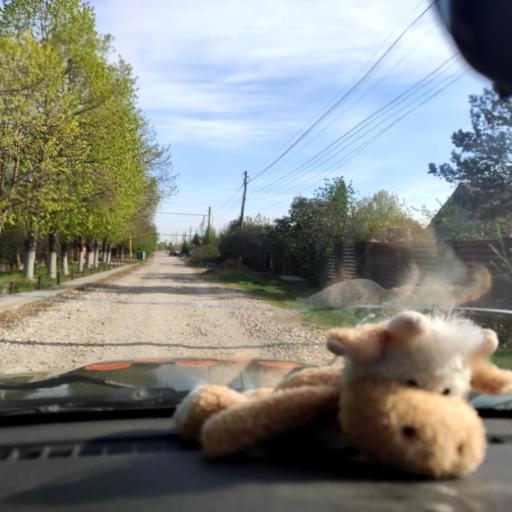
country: RU
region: Samara
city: Tol'yatti
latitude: 53.5713
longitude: 49.3078
